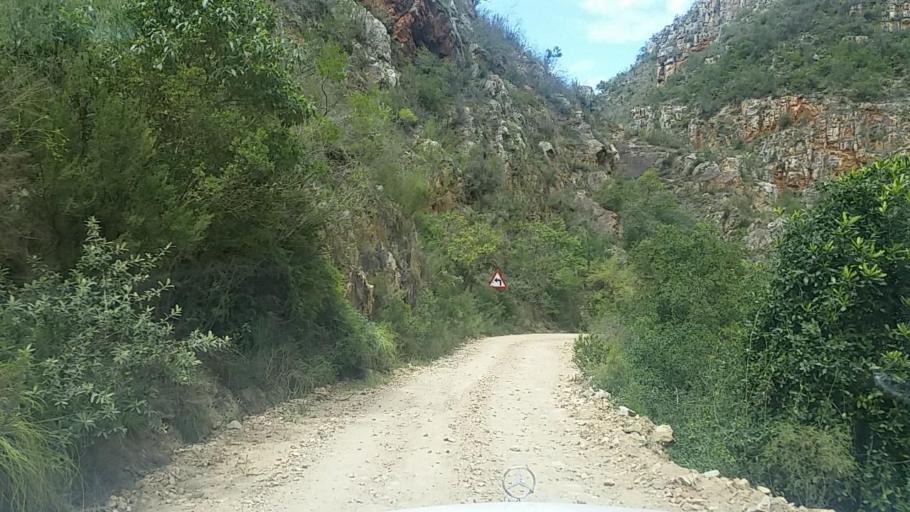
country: ZA
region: Western Cape
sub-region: Eden District Municipality
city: Knysna
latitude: -33.8022
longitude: 23.1804
